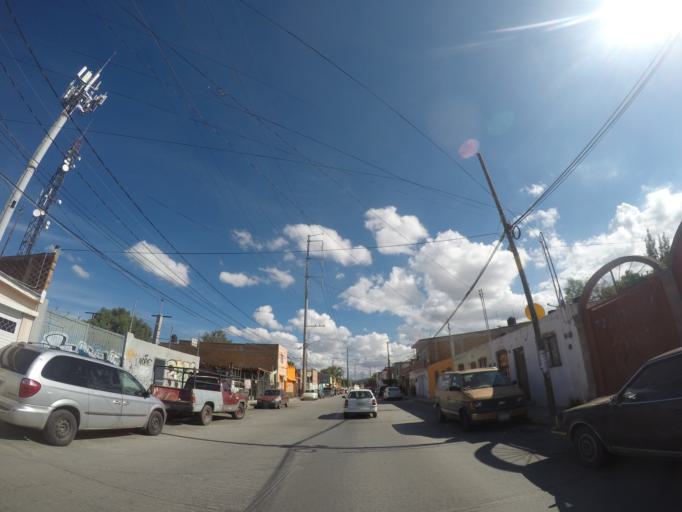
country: MX
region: San Luis Potosi
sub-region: San Luis Potosi
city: San Luis Potosi
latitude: 22.1564
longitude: -100.9683
